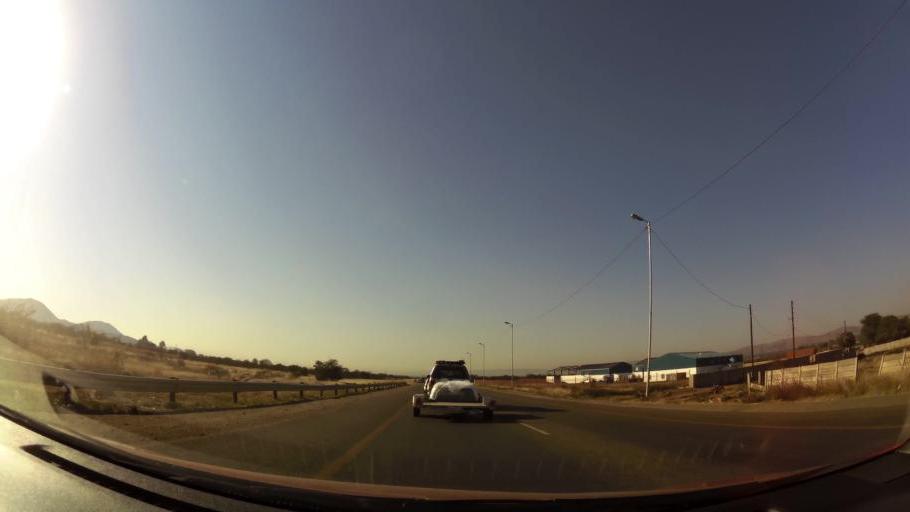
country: ZA
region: Gauteng
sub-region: City of Tshwane Metropolitan Municipality
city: Pretoria
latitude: -25.6366
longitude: 28.1321
